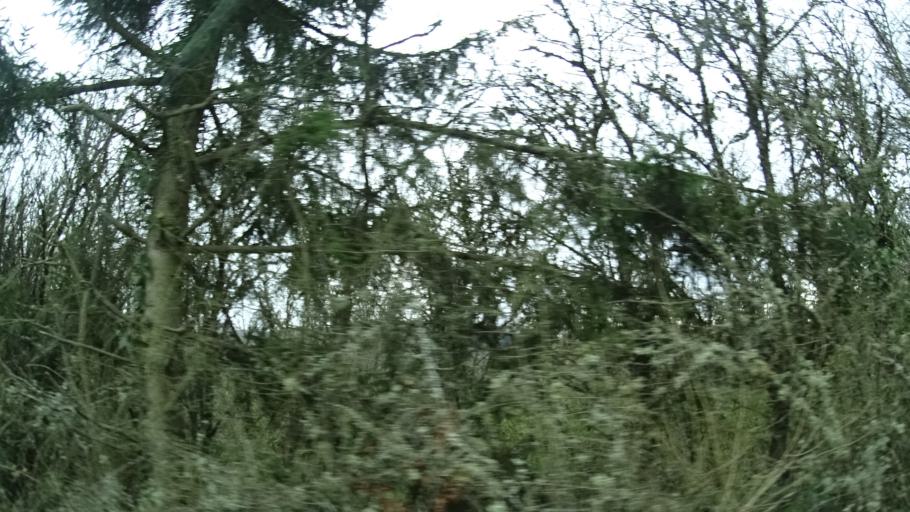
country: DE
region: Rheinland-Pfalz
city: Kirn
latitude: 49.7963
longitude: 7.4468
